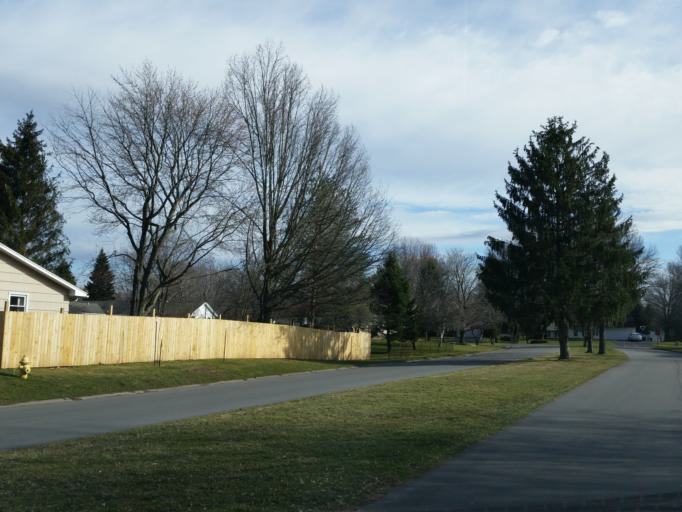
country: US
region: New York
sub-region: Monroe County
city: North Gates
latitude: 43.1253
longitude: -77.7384
